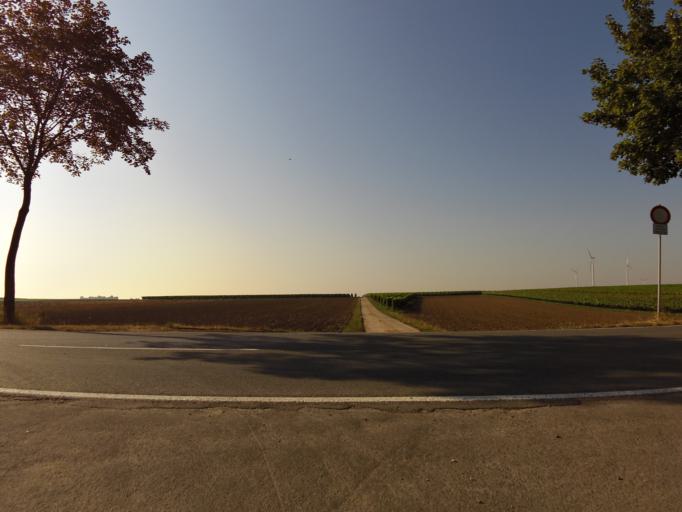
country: DE
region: Rheinland-Pfalz
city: Kleinniedesheim
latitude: 49.6045
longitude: 8.3157
